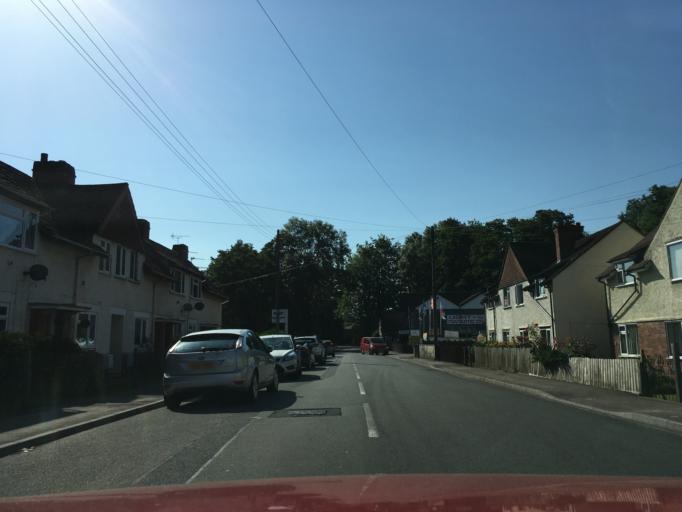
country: GB
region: England
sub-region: Gloucestershire
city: Lydney
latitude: 51.7288
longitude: -2.5336
